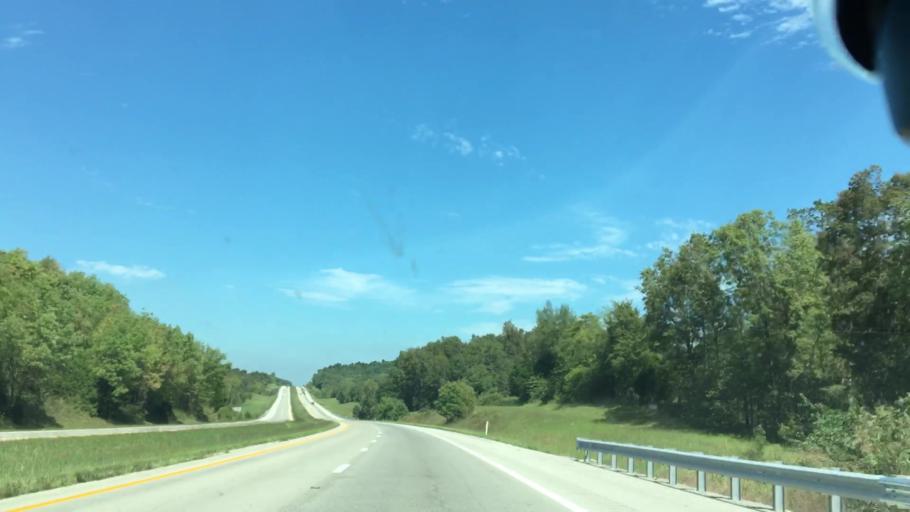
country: US
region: Kentucky
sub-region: Christian County
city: Hopkinsville
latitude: 36.9298
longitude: -87.4704
